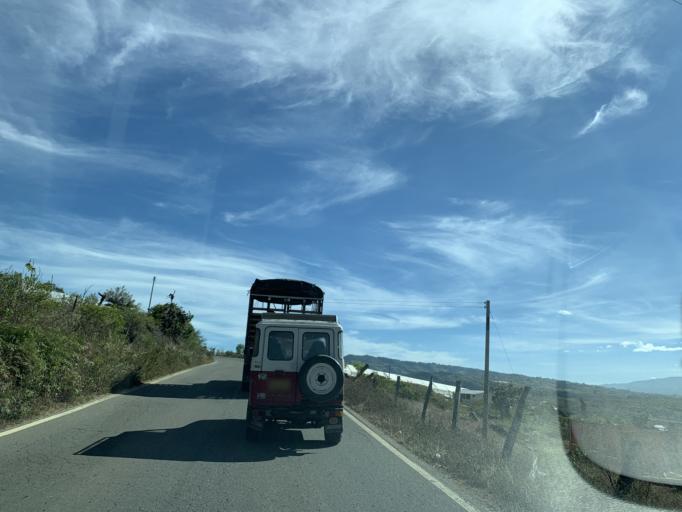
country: CO
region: Boyaca
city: Villa de Leiva
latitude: 5.6745
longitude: -73.5860
